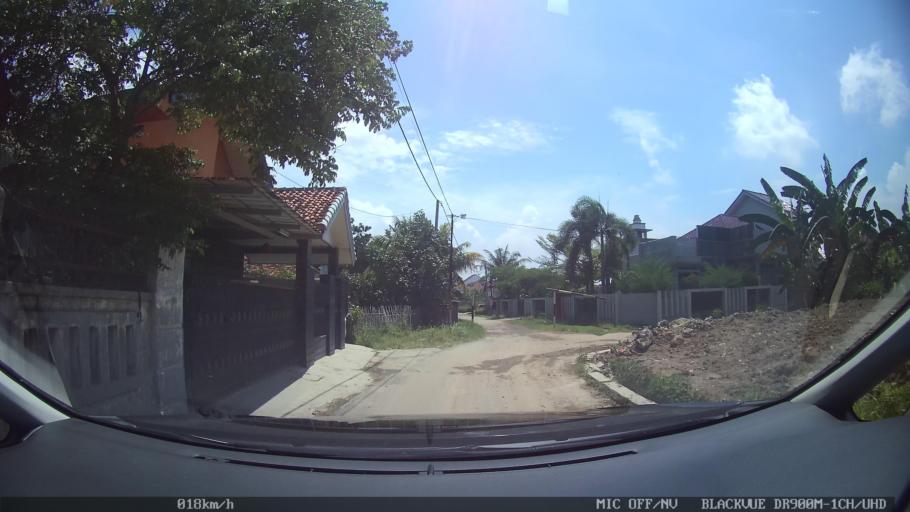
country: ID
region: Lampung
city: Kedaton
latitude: -5.3783
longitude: 105.2922
